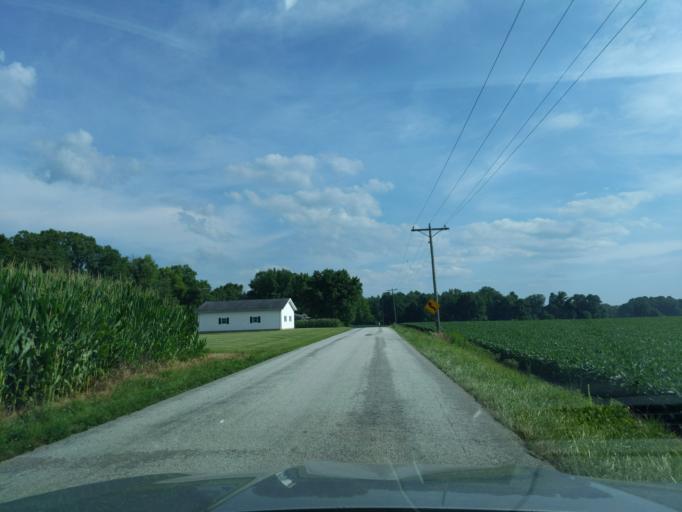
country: US
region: Indiana
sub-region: Decatur County
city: Greensburg
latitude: 39.2505
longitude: -85.4698
